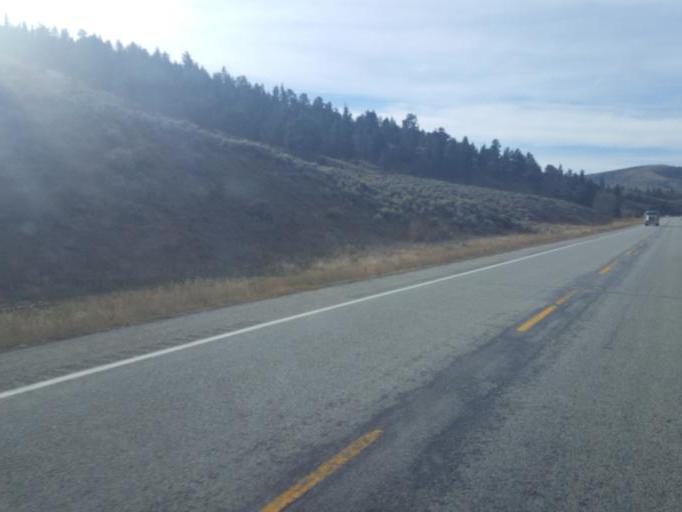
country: US
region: Colorado
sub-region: Costilla County
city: San Luis
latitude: 37.5244
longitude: -105.2985
